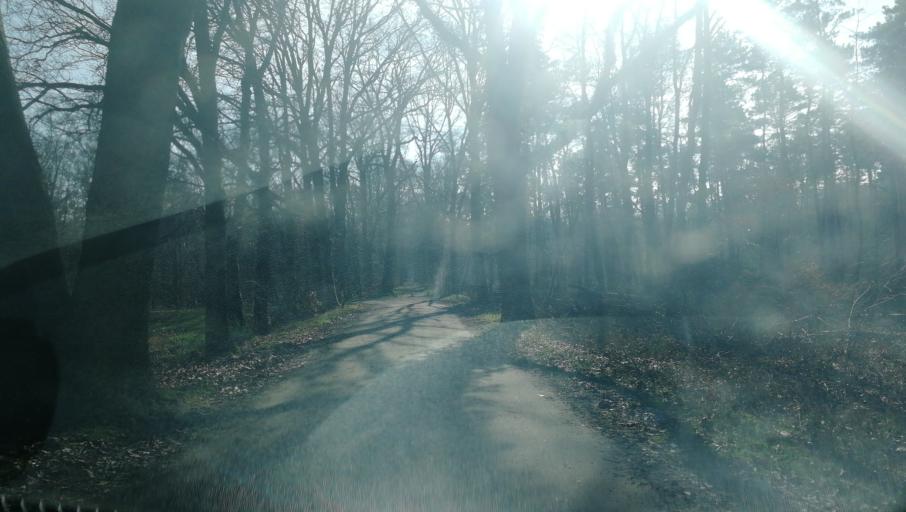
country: NL
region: Limburg
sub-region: Gemeente Venlo
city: Venlo
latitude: 51.4021
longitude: 6.1950
